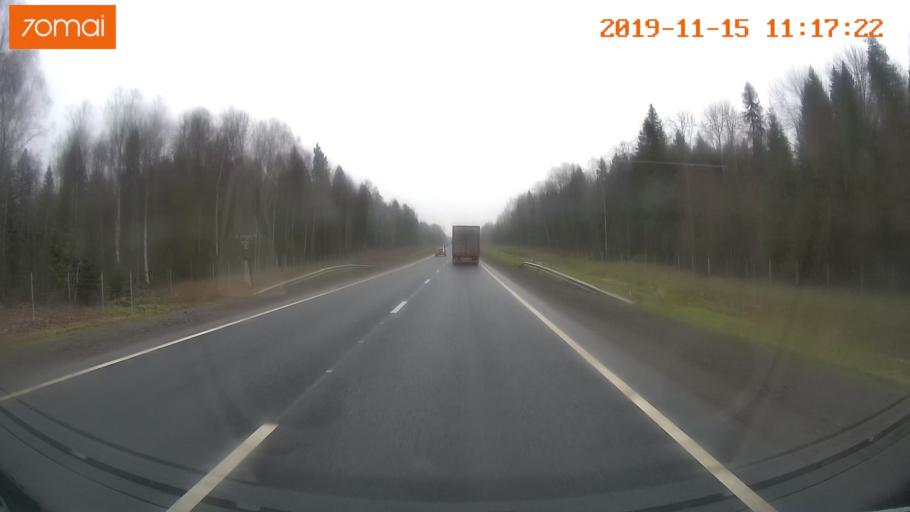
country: RU
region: Vologda
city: Chebsara
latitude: 59.1328
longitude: 39.2491
